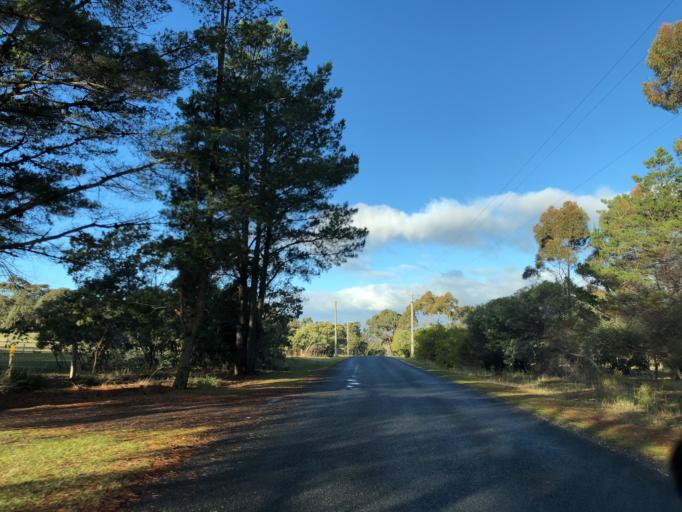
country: AU
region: Victoria
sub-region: Mount Alexander
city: Castlemaine
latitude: -37.2092
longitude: 144.2987
